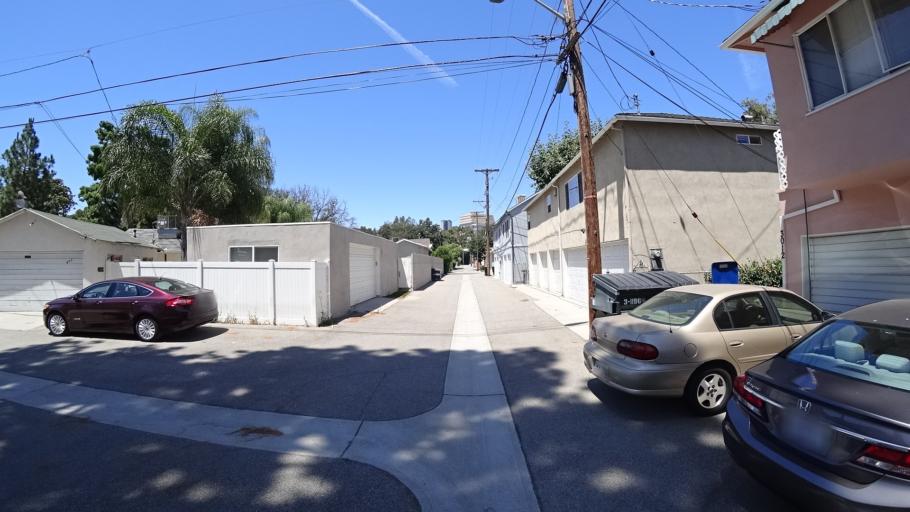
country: US
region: California
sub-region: Los Angeles County
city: Universal City
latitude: 34.1509
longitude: -118.3319
